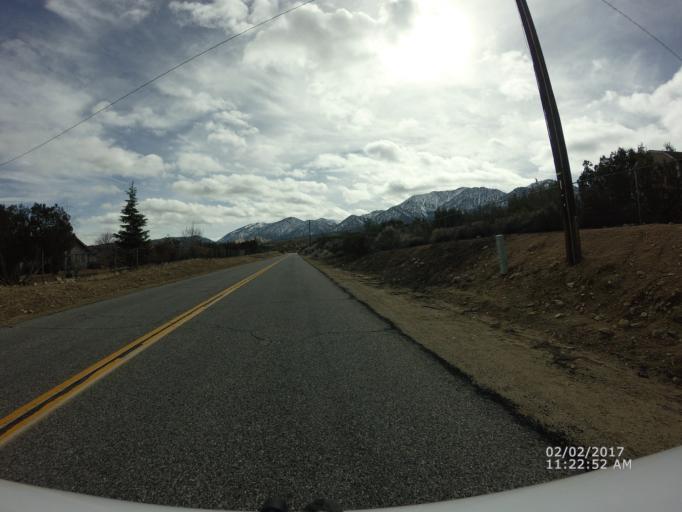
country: US
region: California
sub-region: Los Angeles County
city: Littlerock
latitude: 34.4352
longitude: -117.8827
